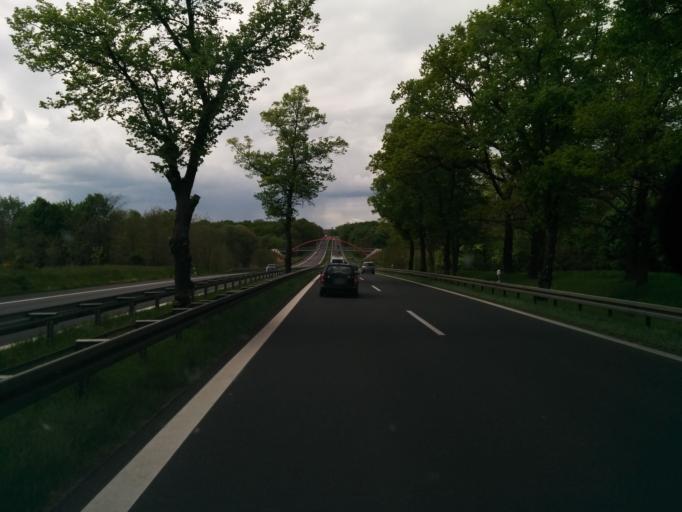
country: DE
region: Brandenburg
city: Dallgow-Doeberitz
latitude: 52.5335
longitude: 13.0215
